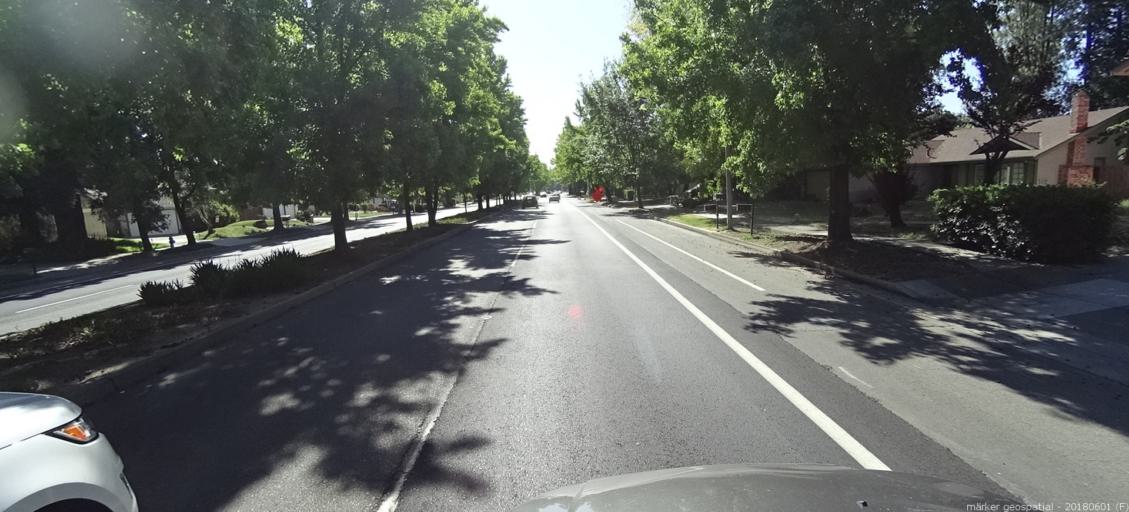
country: US
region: California
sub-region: Sacramento County
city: Parkway
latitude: 38.4968
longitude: -121.5286
